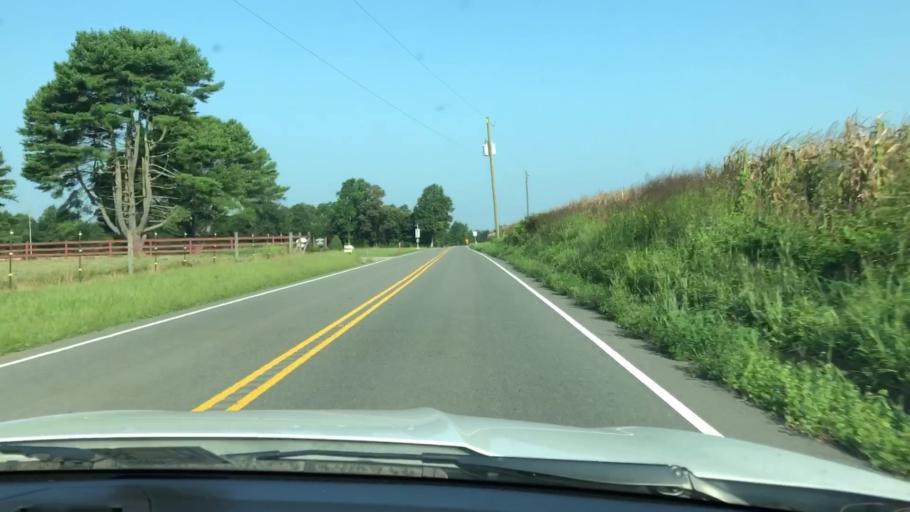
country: US
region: Virginia
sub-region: King William County
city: West Point
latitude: 37.6140
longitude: -76.7848
